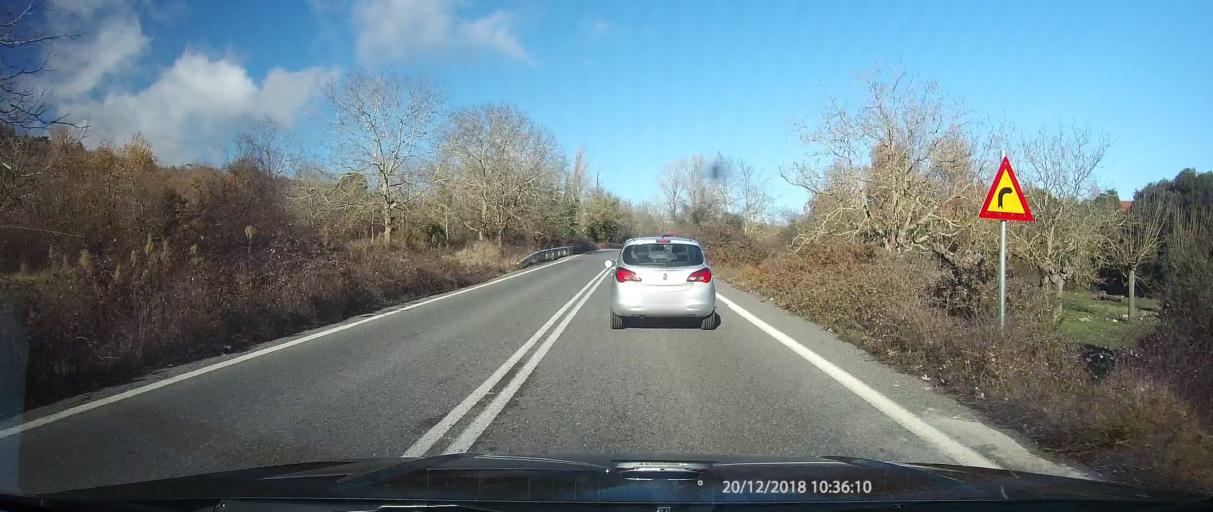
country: GR
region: Peloponnese
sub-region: Nomos Lakonias
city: Kariai
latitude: 37.3628
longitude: 22.4036
